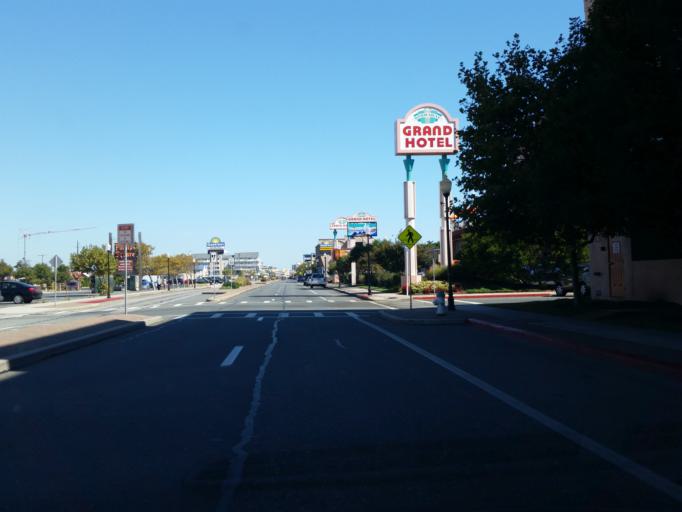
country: US
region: Maryland
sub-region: Worcester County
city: Ocean City
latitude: 38.3500
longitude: -75.0768
